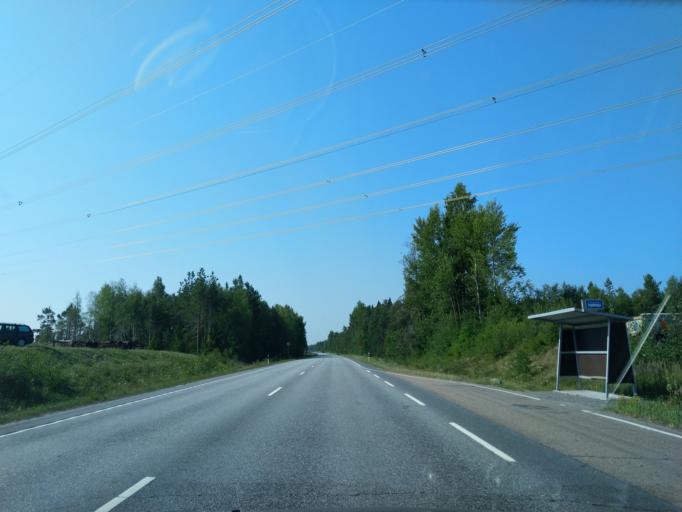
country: FI
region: Satakunta
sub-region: Pori
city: Pomarkku
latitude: 61.6851
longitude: 21.9931
